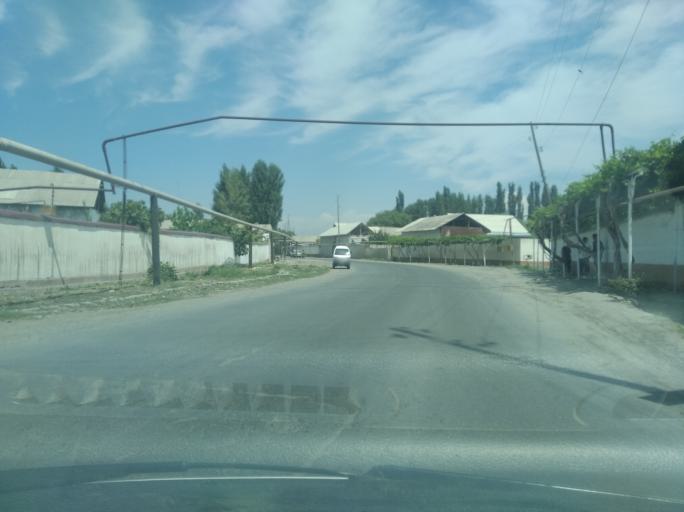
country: UZ
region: Andijon
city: Khujaobod
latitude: 40.6334
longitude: 72.4492
